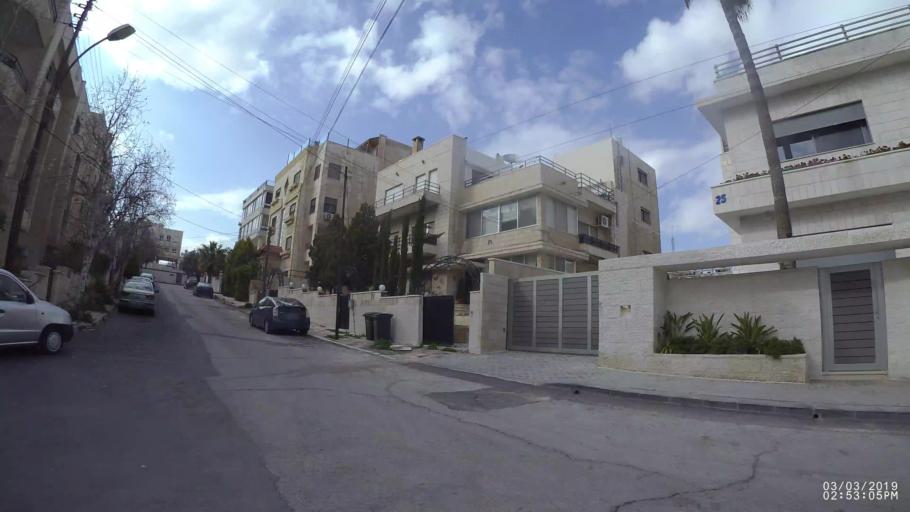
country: JO
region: Amman
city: Amman
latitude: 31.9633
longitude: 35.8949
